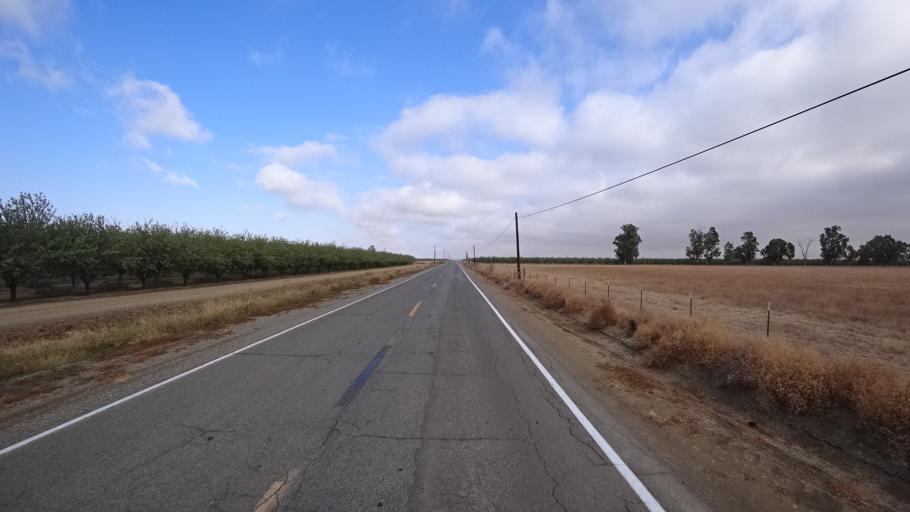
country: US
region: California
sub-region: Yolo County
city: Esparto
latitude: 38.7426
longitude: -122.0074
